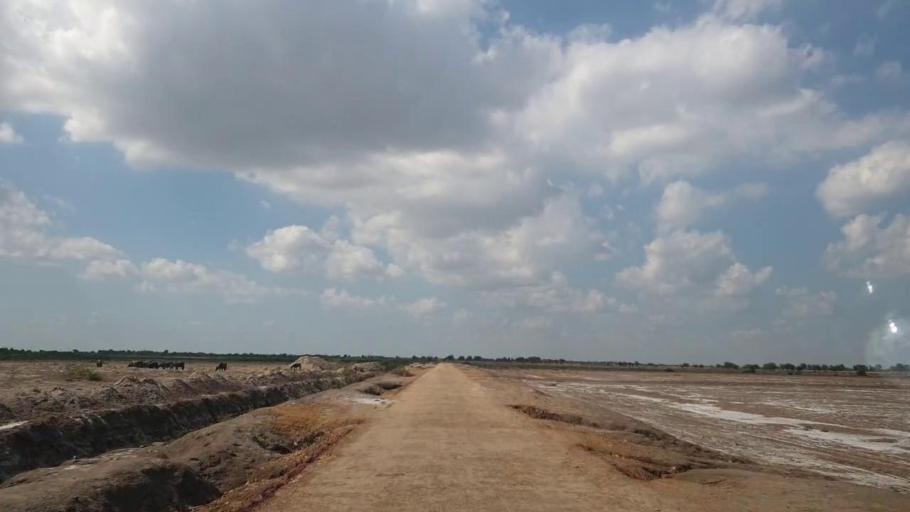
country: PK
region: Sindh
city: Pithoro
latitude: 25.5960
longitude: 69.3590
